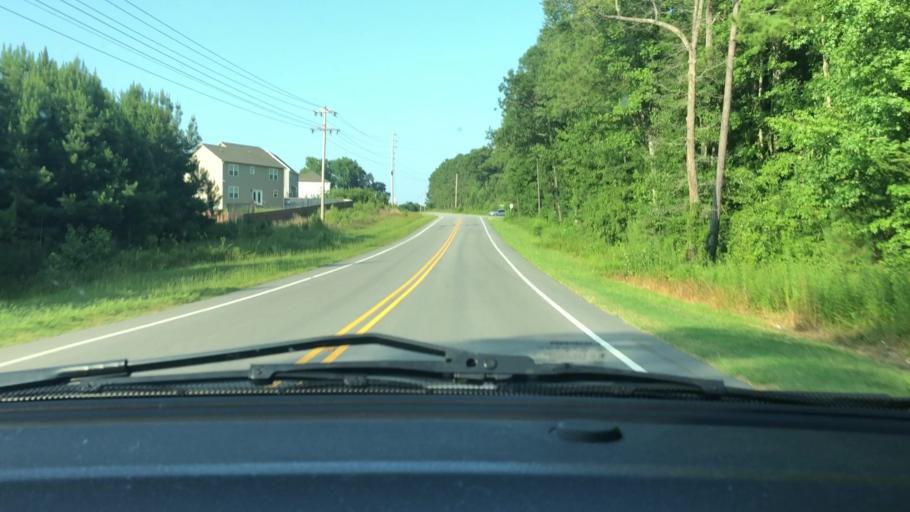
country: US
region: North Carolina
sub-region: Lee County
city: Broadway
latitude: 35.3271
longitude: -79.0614
